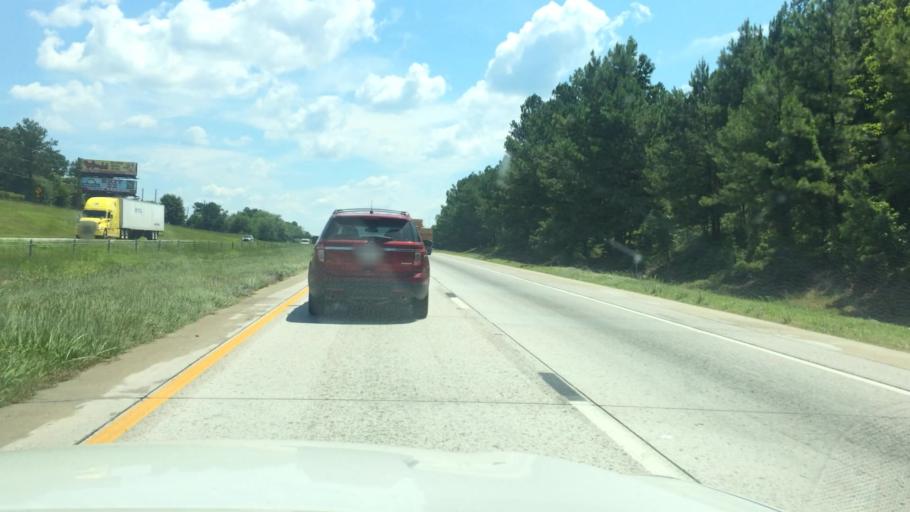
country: US
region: South Carolina
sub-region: Aiken County
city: Belvedere
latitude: 33.5474
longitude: -81.9625
